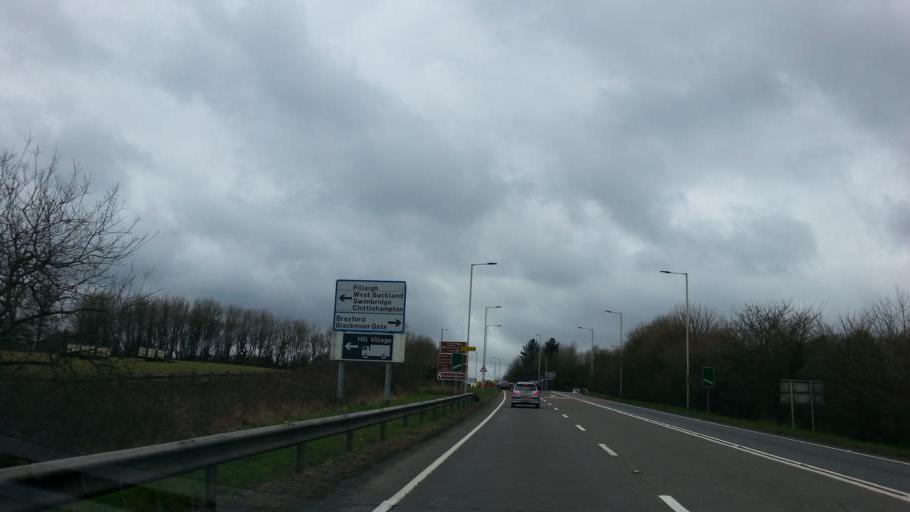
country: GB
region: England
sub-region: Devon
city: South Molton
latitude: 51.0376
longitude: -3.8536
